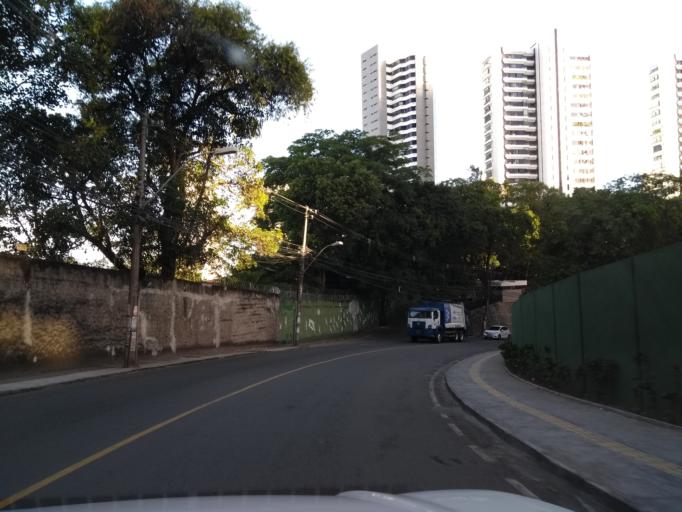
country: BR
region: Bahia
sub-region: Salvador
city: Salvador
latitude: -12.9964
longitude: -38.4866
